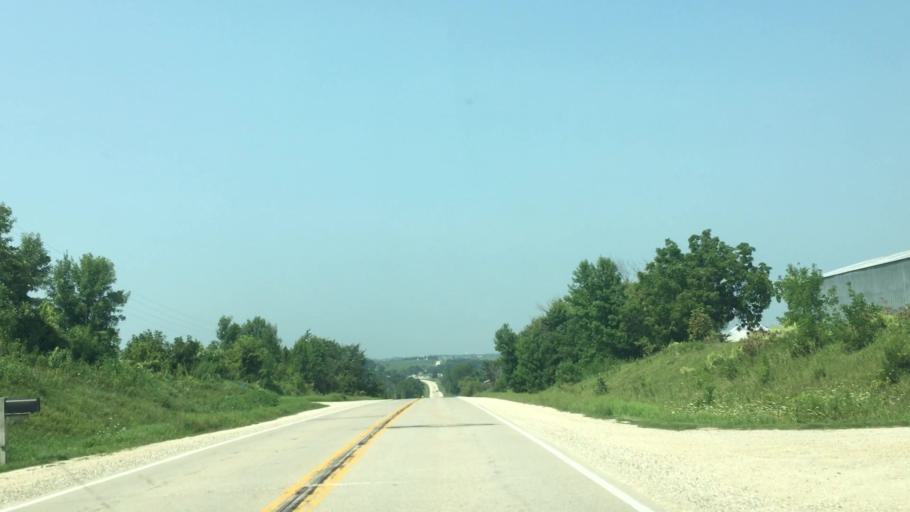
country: US
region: Iowa
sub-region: Fayette County
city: West Union
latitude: 43.1033
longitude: -91.8691
